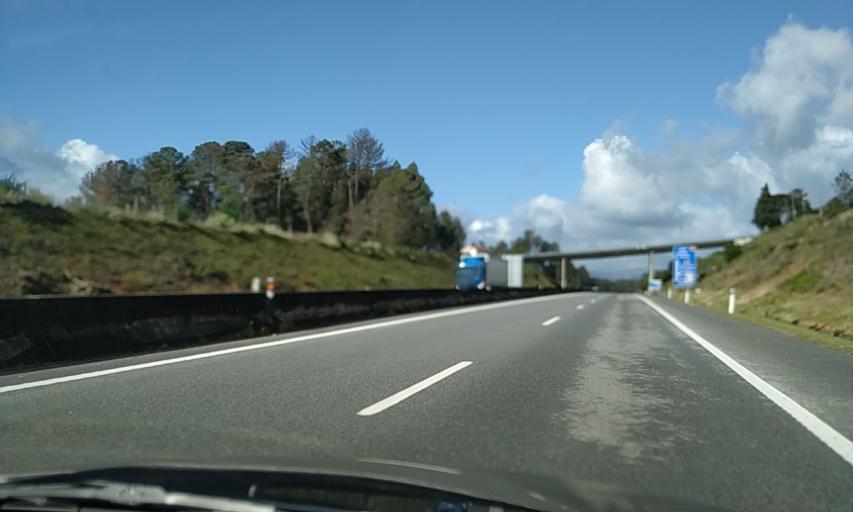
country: PT
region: Viseu
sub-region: Viseu
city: Viseu
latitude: 40.6243
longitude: -7.9403
